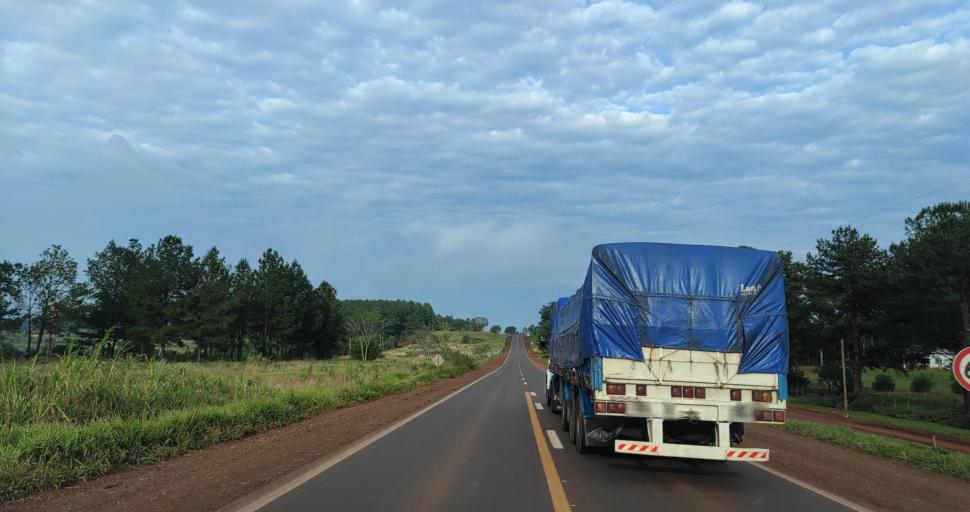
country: AR
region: Corrientes
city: Gobernador Ingeniero Valentin Virasoro
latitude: -27.9415
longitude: -55.9834
